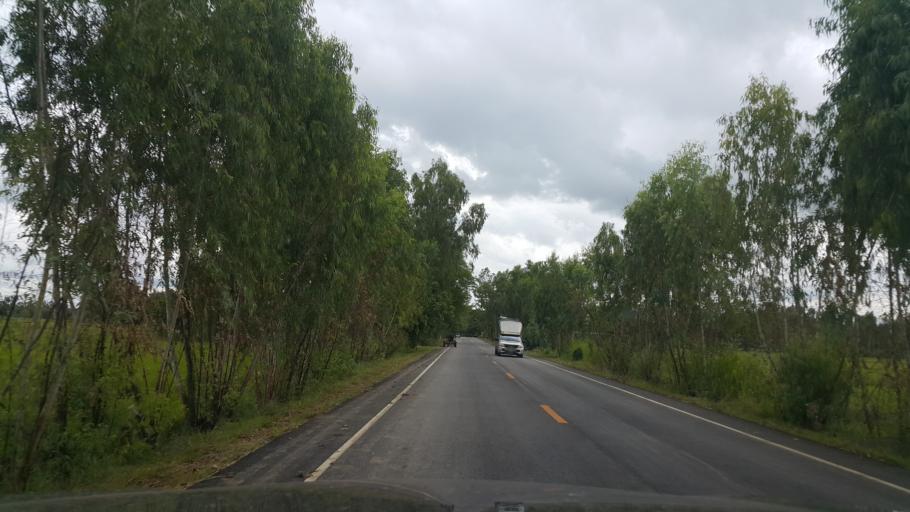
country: TH
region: Sukhothai
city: Kong Krailat
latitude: 16.9151
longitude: 99.8866
